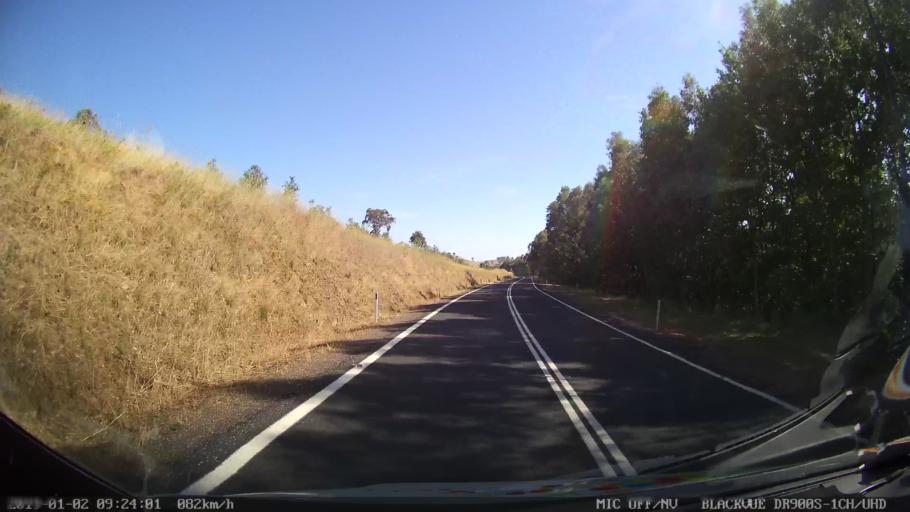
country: AU
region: New South Wales
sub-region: Tumut Shire
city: Tumut
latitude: -35.3825
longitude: 148.2914
